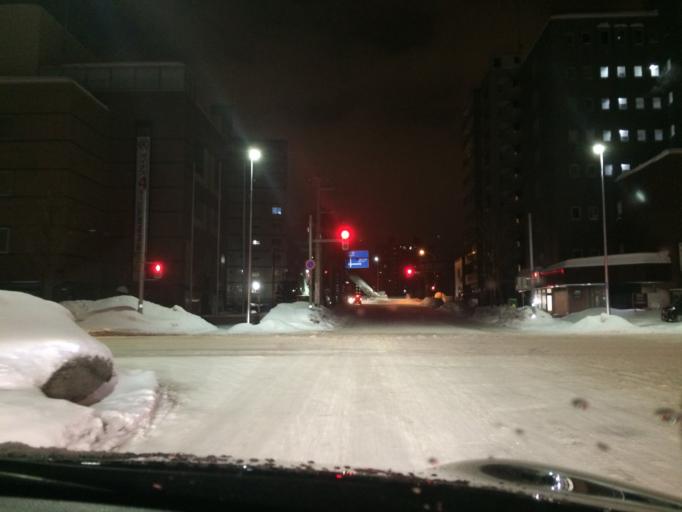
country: JP
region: Hokkaido
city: Sapporo
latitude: 43.0650
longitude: 141.3728
